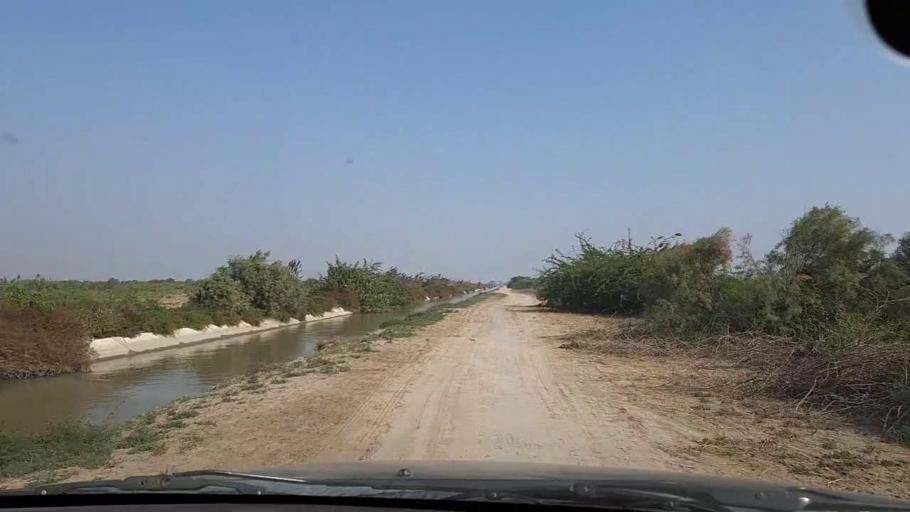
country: PK
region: Sindh
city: Mirpur Sakro
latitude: 24.3419
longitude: 67.7113
